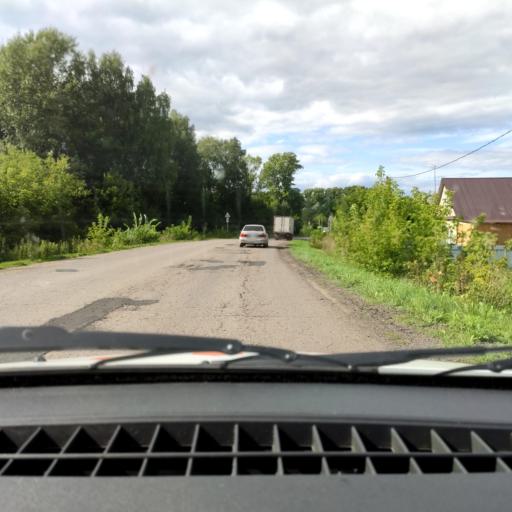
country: RU
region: Bashkortostan
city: Iglino
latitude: 54.8778
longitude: 56.5522
